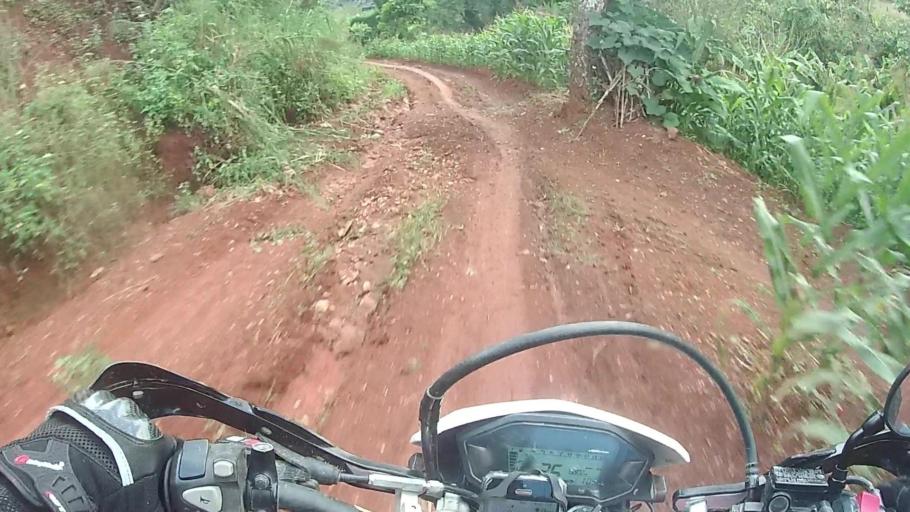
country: TH
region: Lampang
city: Wang Nuea
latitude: 19.0686
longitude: 99.4788
